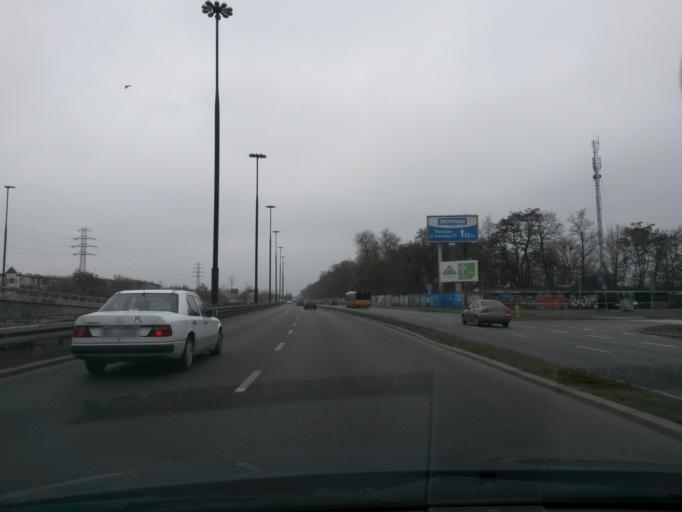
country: PL
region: Masovian Voivodeship
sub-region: Warszawa
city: Mokotow
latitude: 52.1656
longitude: 21.0173
